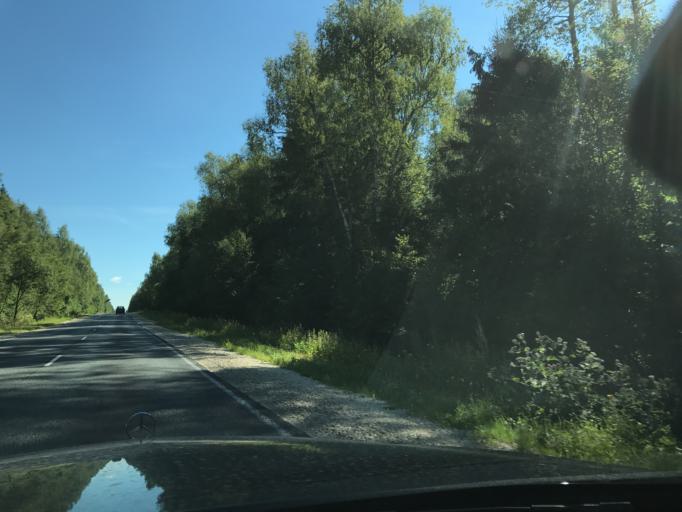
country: RU
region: Vladimir
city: Kol'chugino
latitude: 56.2838
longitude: 39.2916
